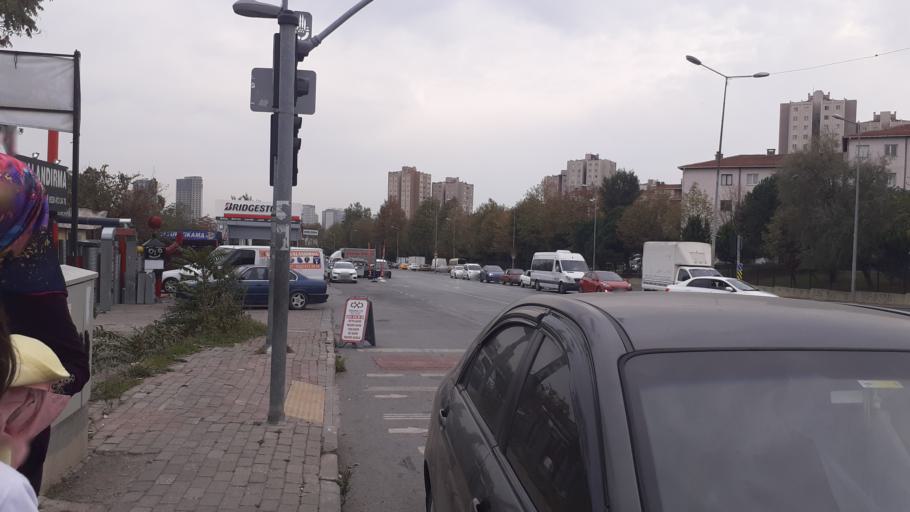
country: TR
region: Istanbul
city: Mahmutbey
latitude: 41.0491
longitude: 28.7977
